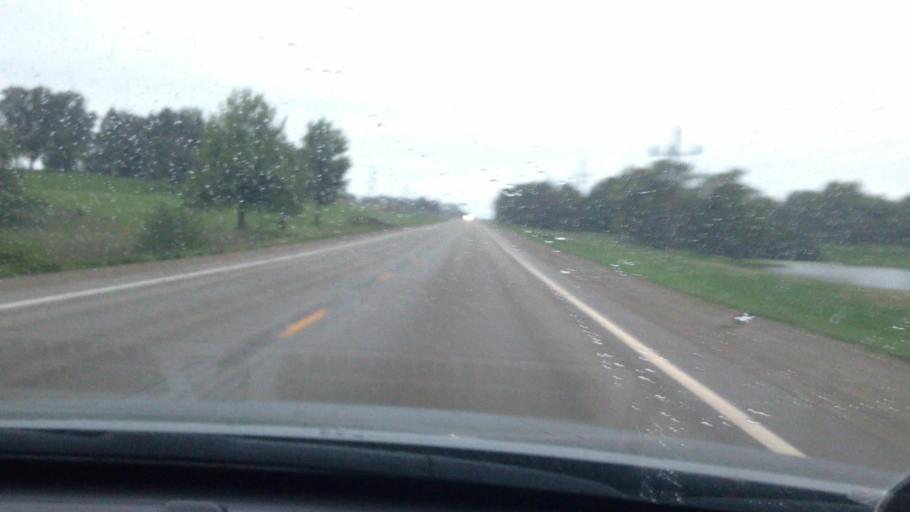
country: US
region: Kansas
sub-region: Brown County
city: Hiawatha
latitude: 39.8266
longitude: -95.5270
